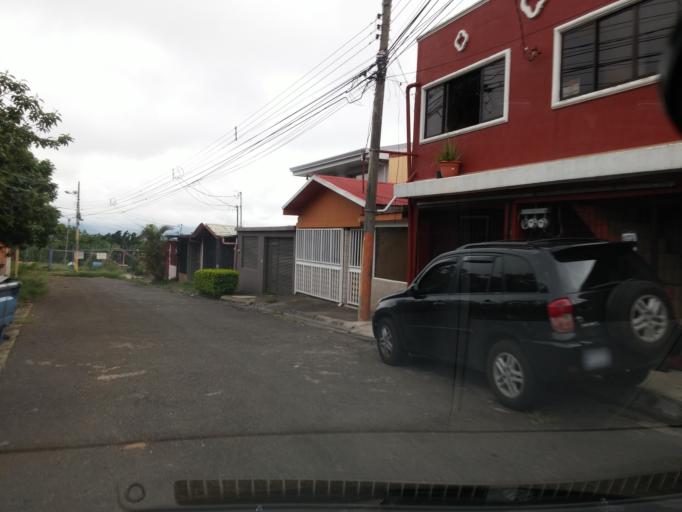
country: CR
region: Heredia
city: San Josecito
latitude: 10.0216
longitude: -84.1026
